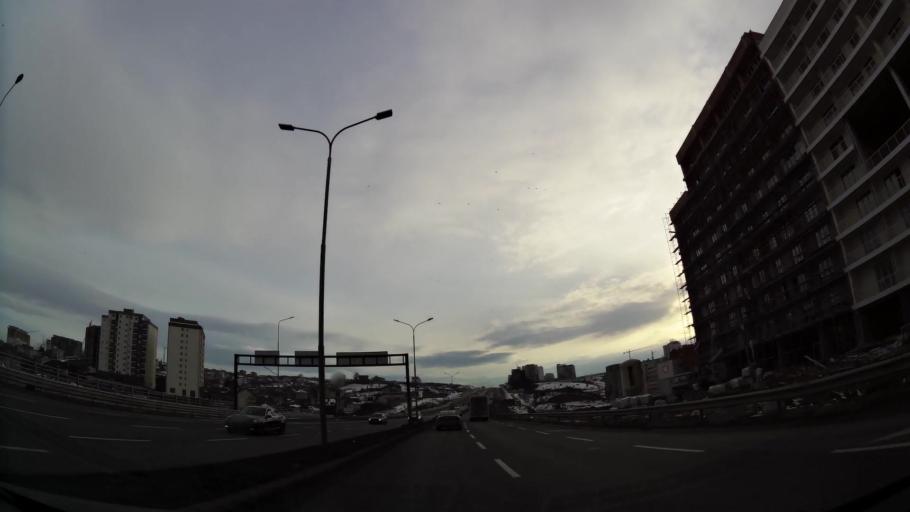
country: XK
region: Pristina
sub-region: Komuna e Prishtines
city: Pristina
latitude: 42.6425
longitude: 21.1559
